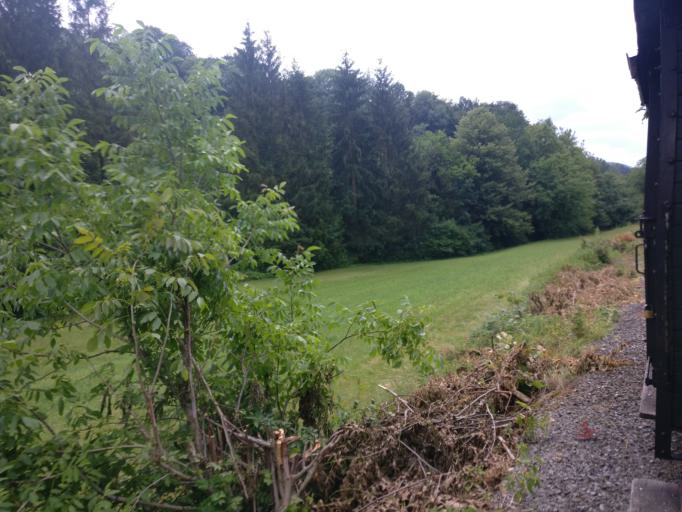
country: AT
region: Upper Austria
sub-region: Politischer Bezirk Kirchdorf an der Krems
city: Gruenburg
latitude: 47.9836
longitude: 14.2764
